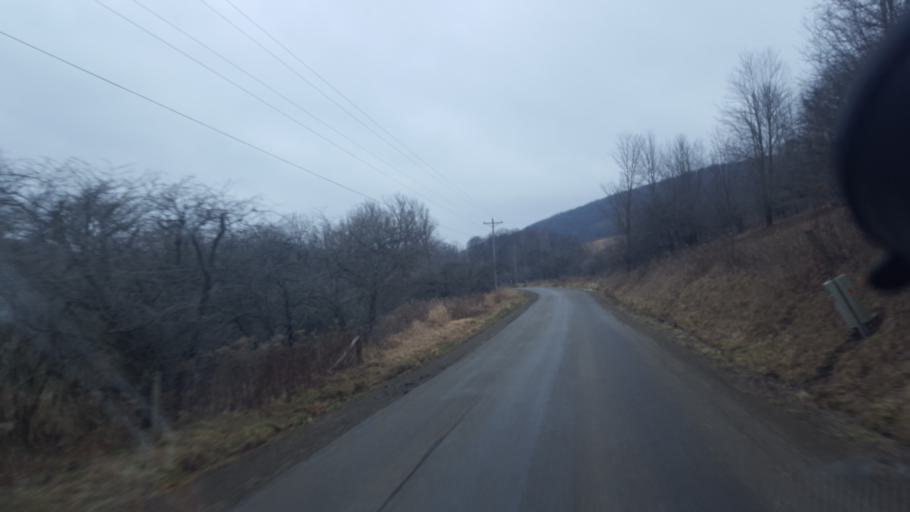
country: US
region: Pennsylvania
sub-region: Tioga County
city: Westfield
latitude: 41.9628
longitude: -77.7106
